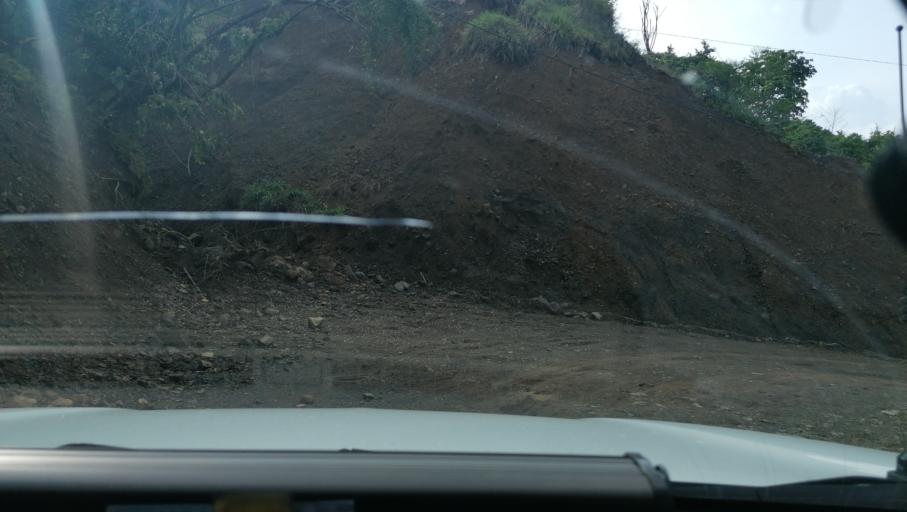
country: MX
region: Chiapas
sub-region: Tapilula
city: San Francisco Jacona
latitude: 17.3113
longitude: -93.1009
